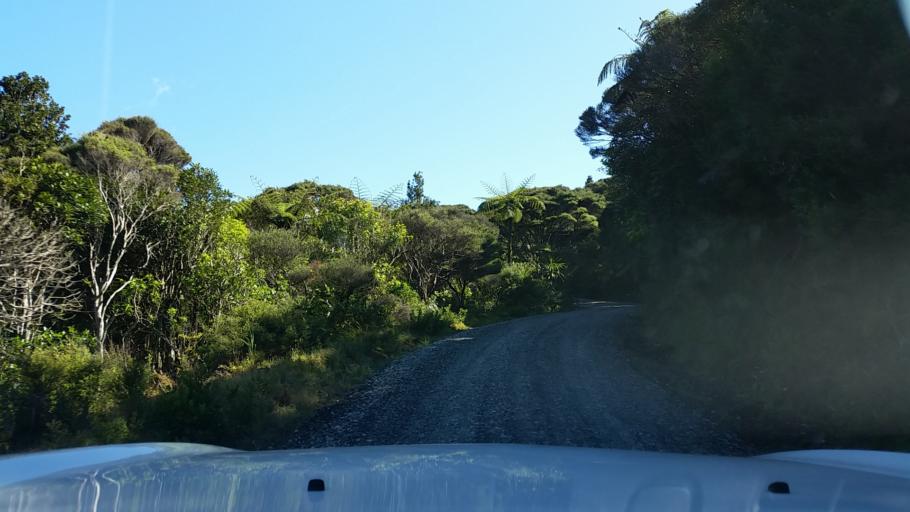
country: NZ
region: Auckland
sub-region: Auckland
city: Titirangi
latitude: -37.0175
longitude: 174.5372
